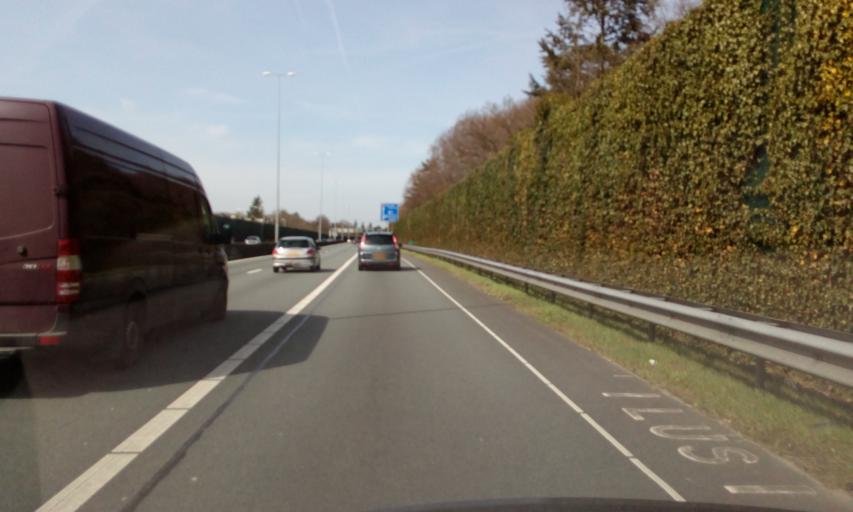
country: NL
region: North Holland
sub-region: Gemeente Bussum
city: Bussum
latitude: 52.2729
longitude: 5.1934
